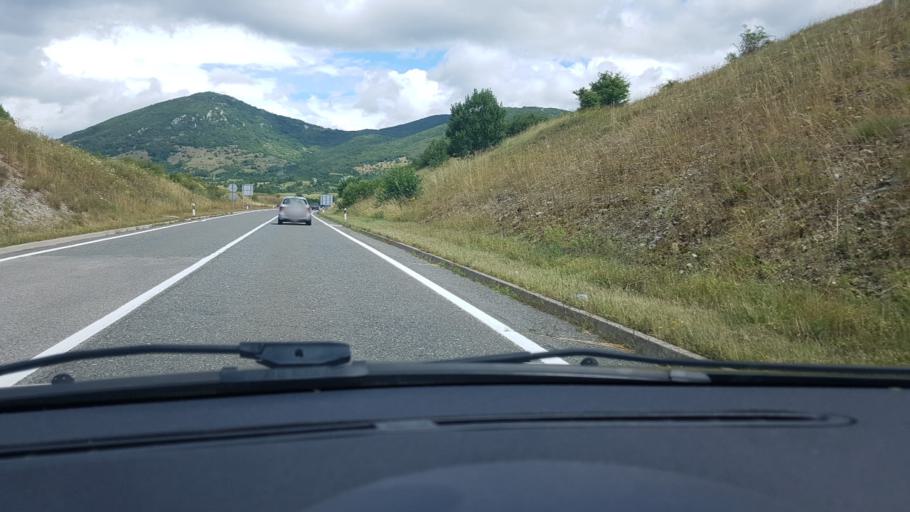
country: HR
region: Zadarska
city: Gracac
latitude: 44.5064
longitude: 15.7524
